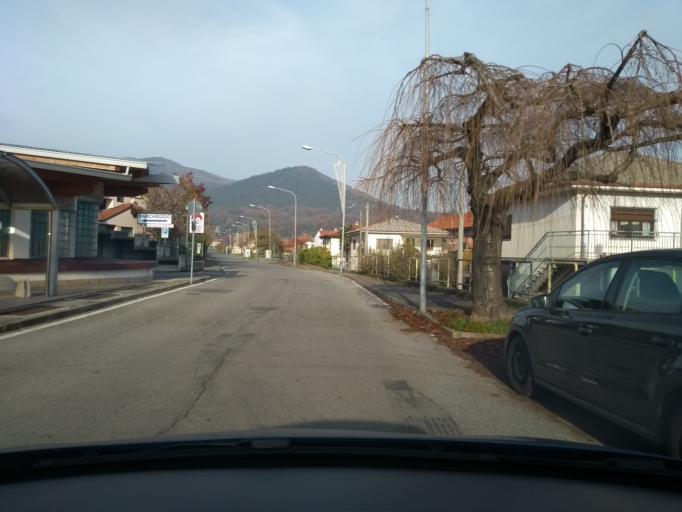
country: IT
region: Piedmont
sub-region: Provincia di Torino
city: Balangero
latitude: 45.2664
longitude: 7.5214
